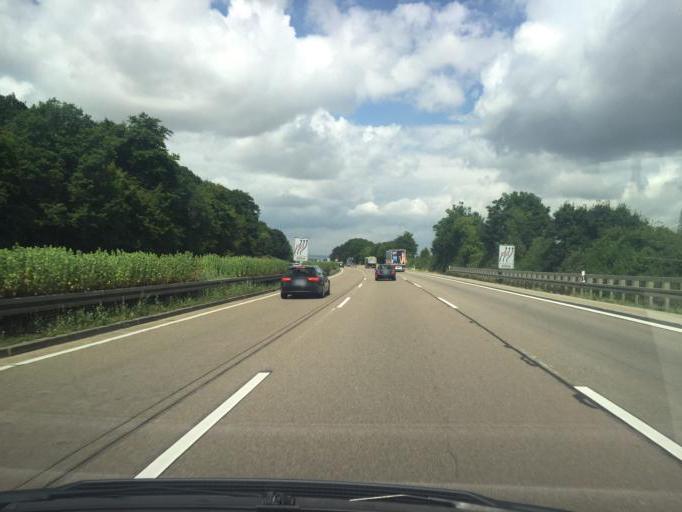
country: DE
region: Hesse
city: Bad Camberg
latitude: 50.3260
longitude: 8.2160
